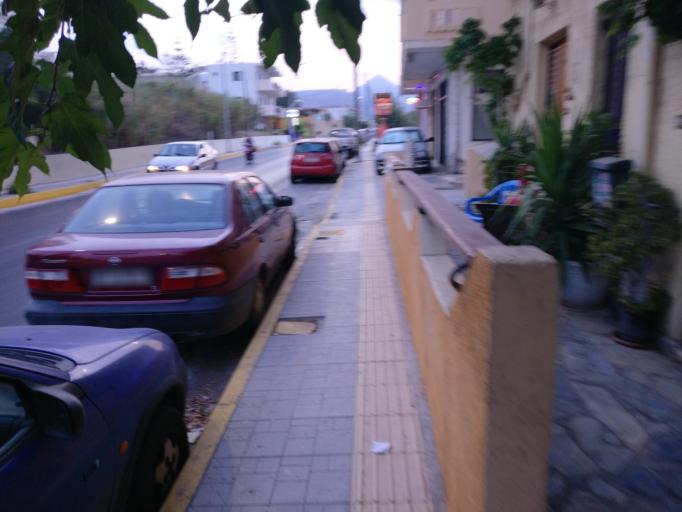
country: GR
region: Crete
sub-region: Nomos Irakleiou
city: Gazi
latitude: 35.3354
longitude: 25.0873
